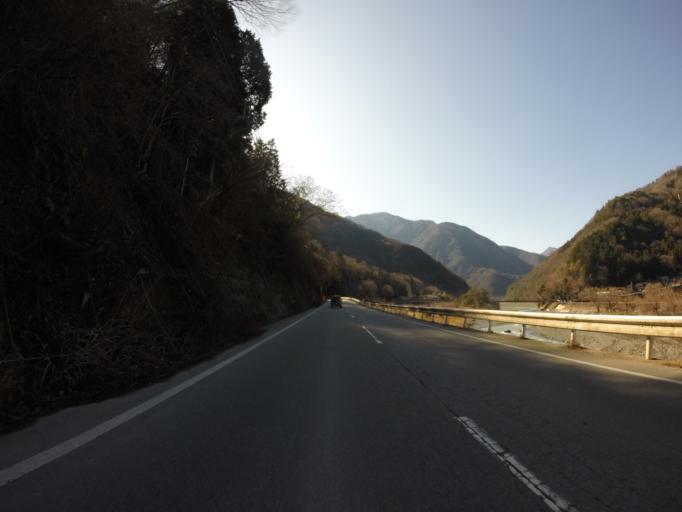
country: JP
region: Yamanashi
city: Ryuo
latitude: 35.4197
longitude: 138.3853
